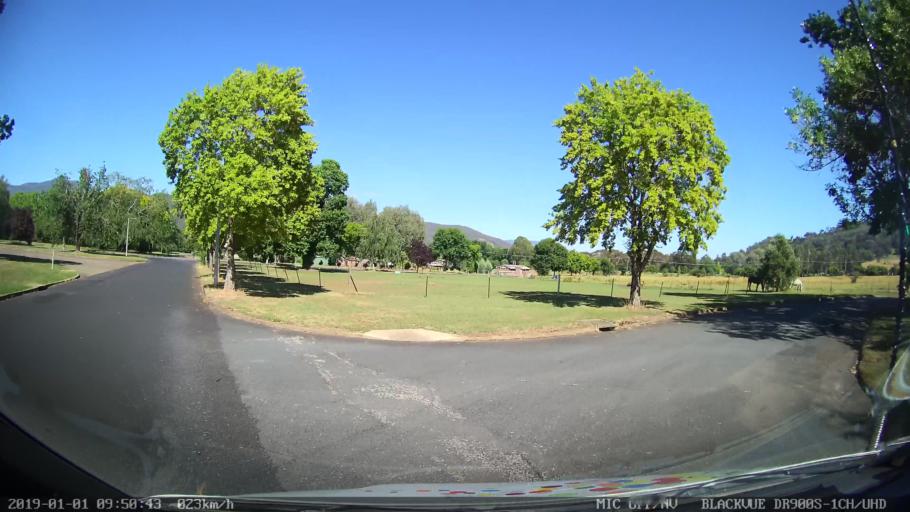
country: AU
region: New South Wales
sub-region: Snowy River
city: Jindabyne
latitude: -36.2167
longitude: 148.1249
